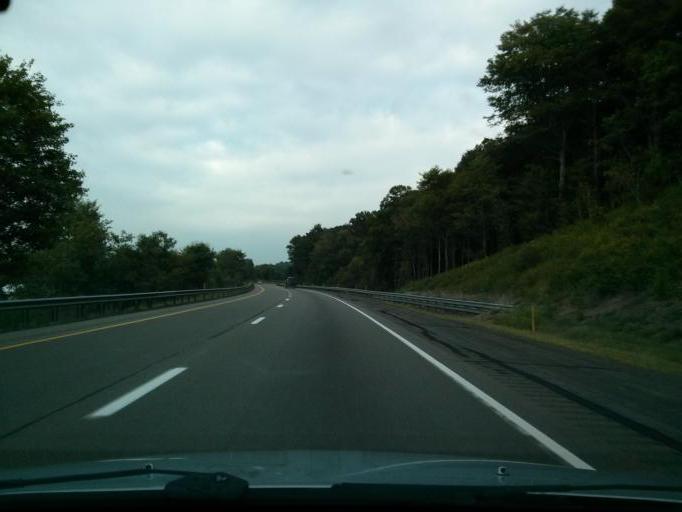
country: US
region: Pennsylvania
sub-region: Jefferson County
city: Brookville
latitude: 41.1692
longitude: -79.0225
